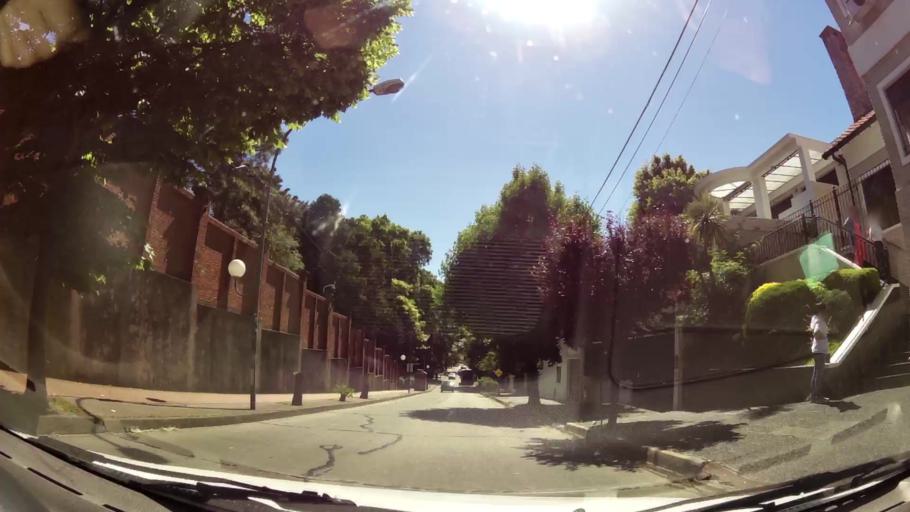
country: AR
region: Buenos Aires
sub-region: Partido de Vicente Lopez
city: Olivos
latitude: -34.5149
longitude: -58.4794
